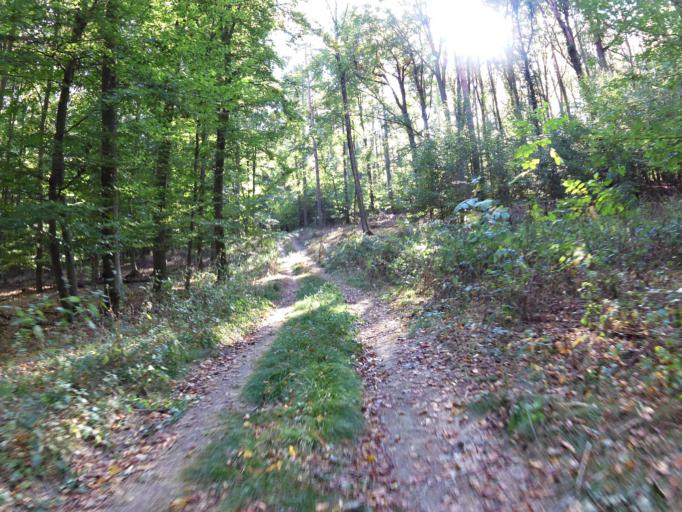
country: DE
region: Bavaria
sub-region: Regierungsbezirk Unterfranken
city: Eibelstadt
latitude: 49.7270
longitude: 9.9815
